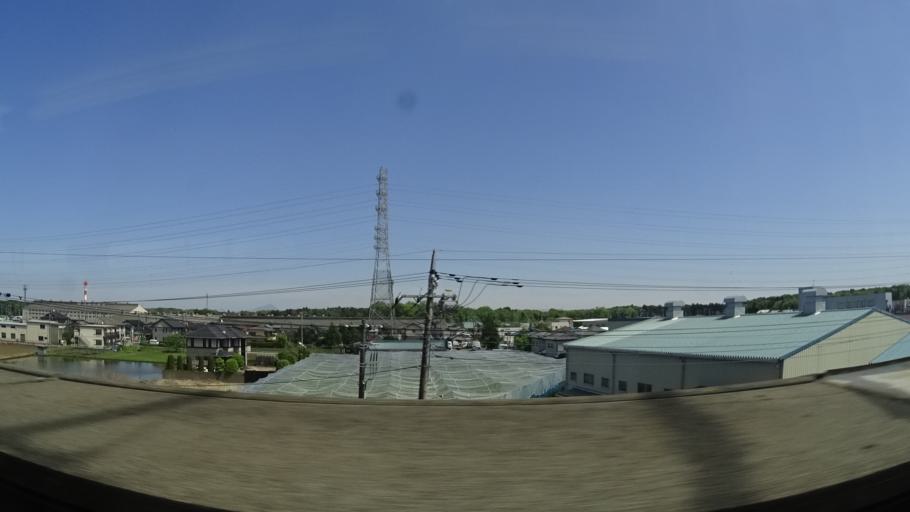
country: JP
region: Tochigi
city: Oyama
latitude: 36.2851
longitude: 139.7845
